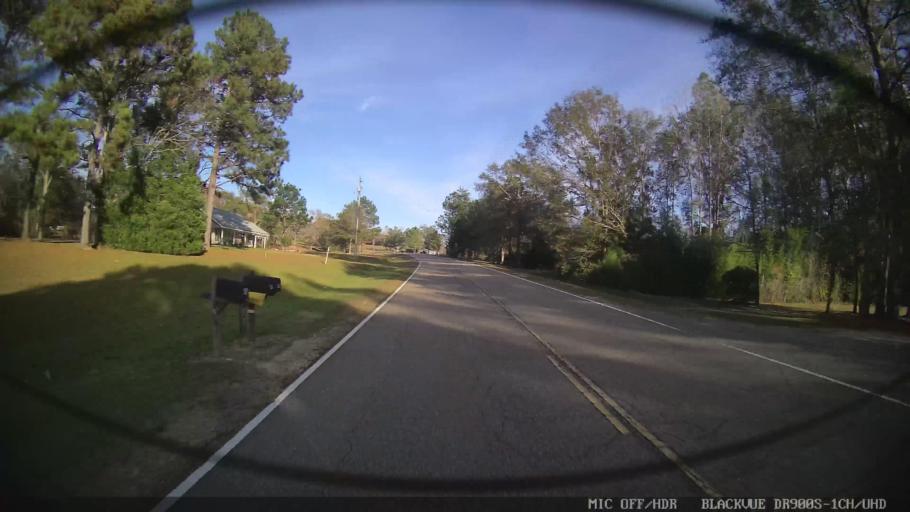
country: US
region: Mississippi
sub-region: Lamar County
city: Purvis
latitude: 31.1661
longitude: -89.3090
